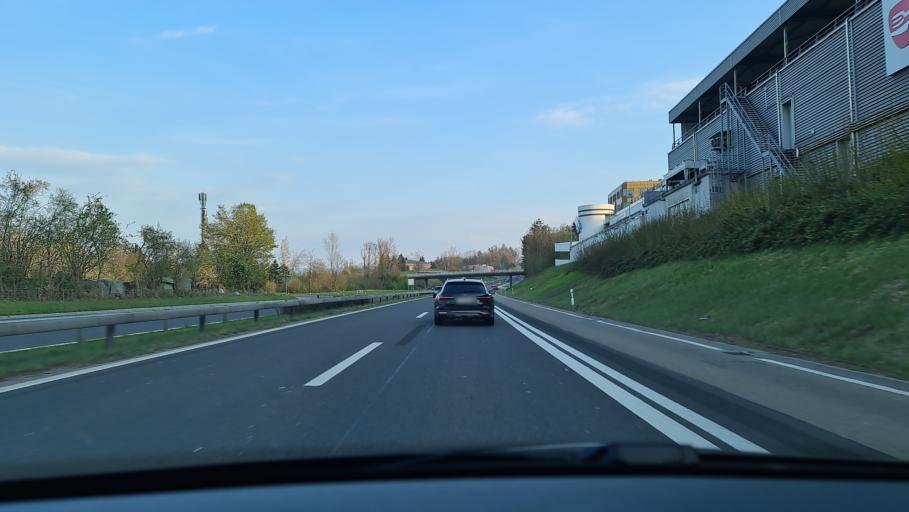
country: CH
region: Zurich
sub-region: Bezirk Horgen
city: Ruschlikon
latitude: 47.3040
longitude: 8.5463
